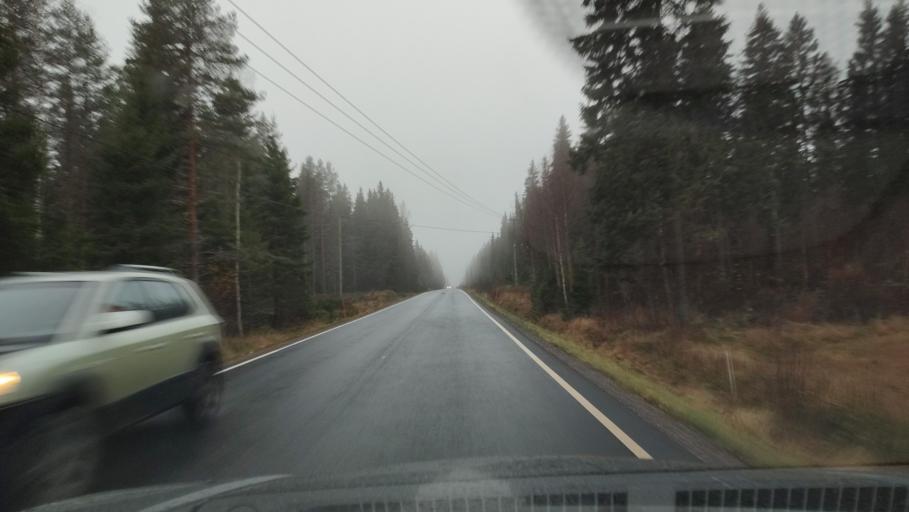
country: FI
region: Southern Ostrobothnia
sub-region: Suupohja
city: Karijoki
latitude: 62.1811
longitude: 21.7761
